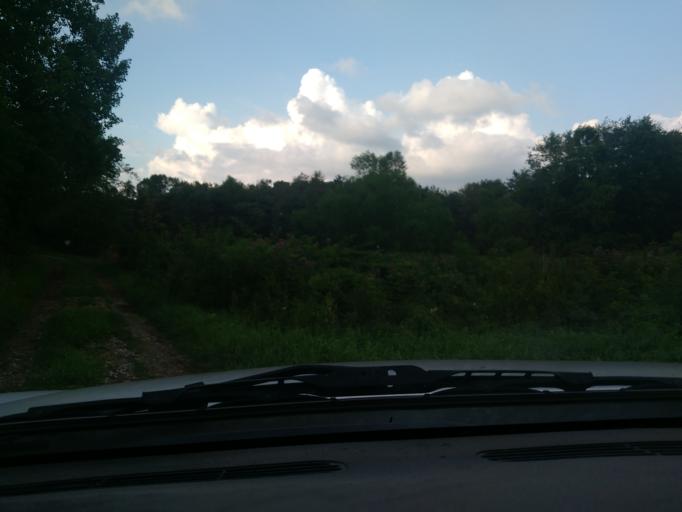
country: US
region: Ohio
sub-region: Knox County
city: Oak Hill
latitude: 40.2601
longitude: -82.2550
